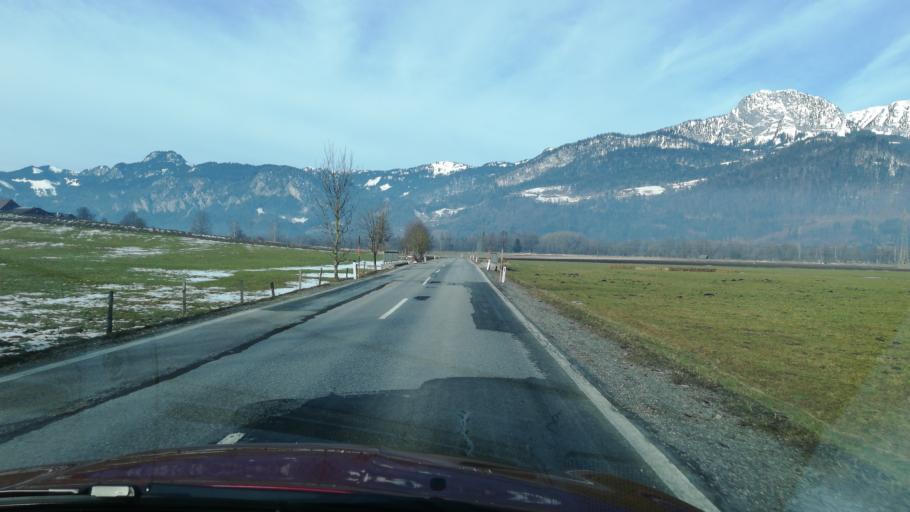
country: AT
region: Styria
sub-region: Politischer Bezirk Liezen
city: Weissenbach bei Liezen
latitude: 47.5454
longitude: 14.1997
